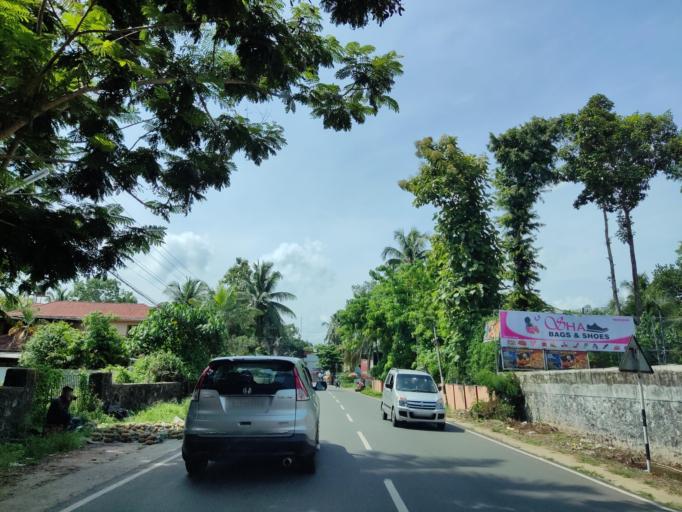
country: IN
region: Kerala
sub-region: Alappuzha
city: Mavelikara
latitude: 9.3150
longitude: 76.5340
